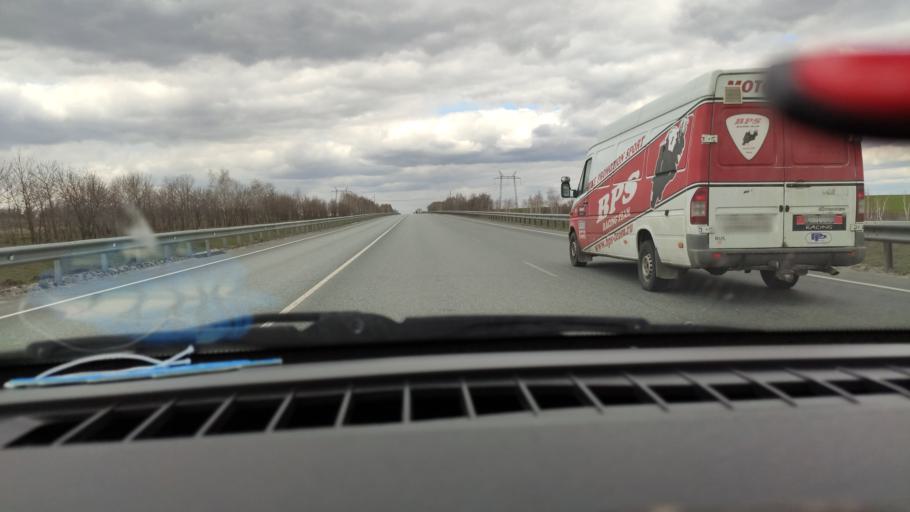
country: RU
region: Saratov
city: Tersa
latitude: 52.1013
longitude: 47.5088
